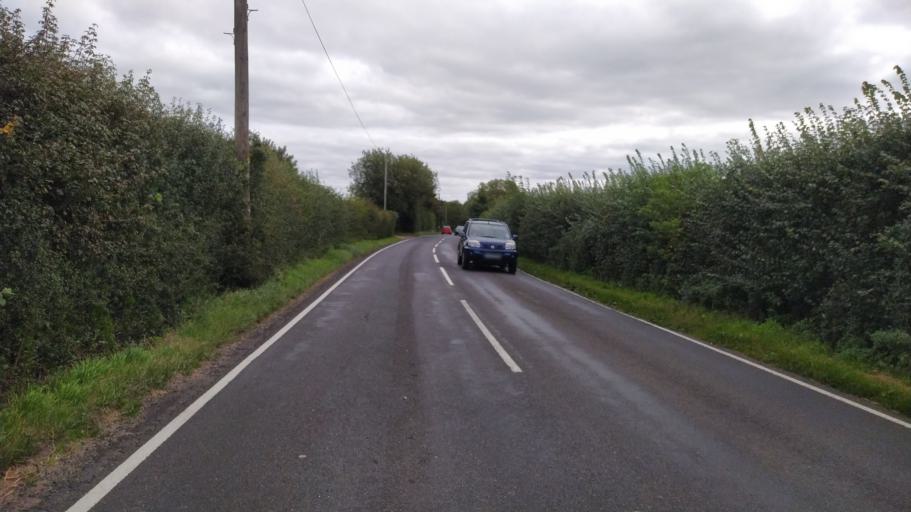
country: GB
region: England
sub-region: Dorset
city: Gillingham
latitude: 51.0448
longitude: -2.3109
